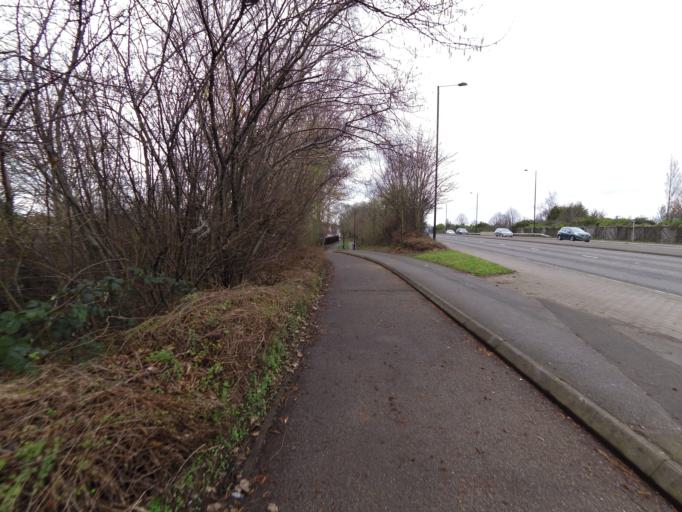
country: GB
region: England
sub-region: Doncaster
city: Bentley
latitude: 53.5337
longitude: -1.1573
